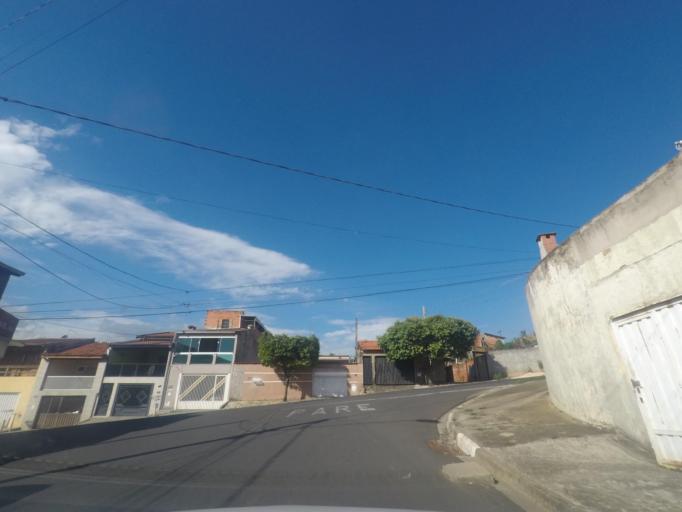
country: BR
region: Sao Paulo
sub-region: Sumare
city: Sumare
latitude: -22.8115
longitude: -47.2679
